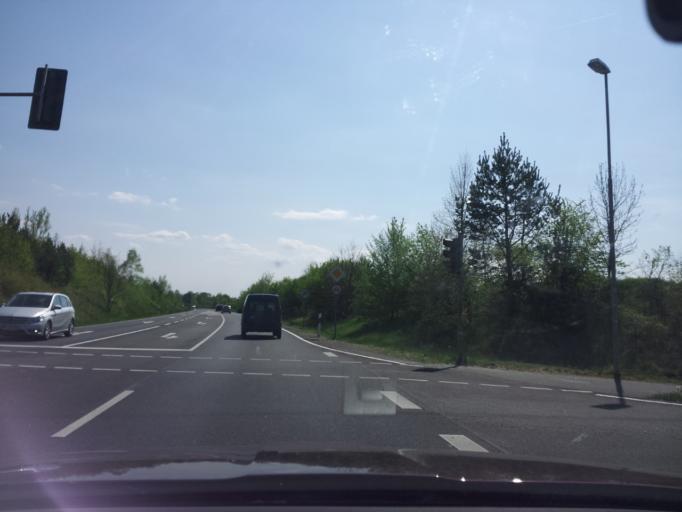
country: DE
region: Brandenburg
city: Beelitz
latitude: 52.2495
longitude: 12.9849
